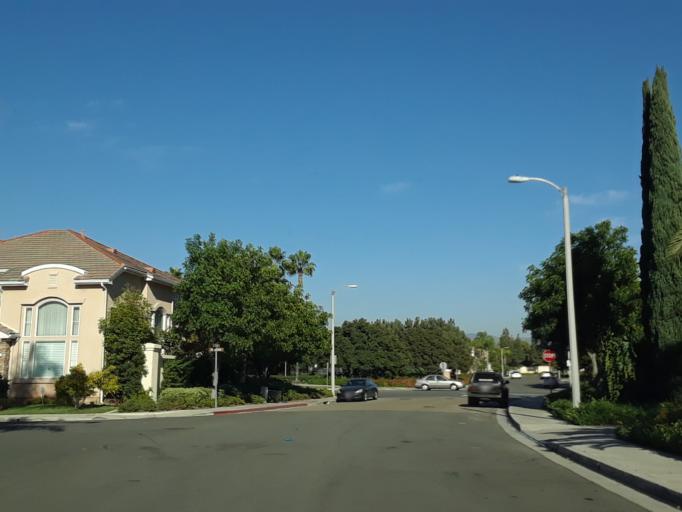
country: US
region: California
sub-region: Orange County
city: Irvine
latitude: 33.6957
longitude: -117.8043
